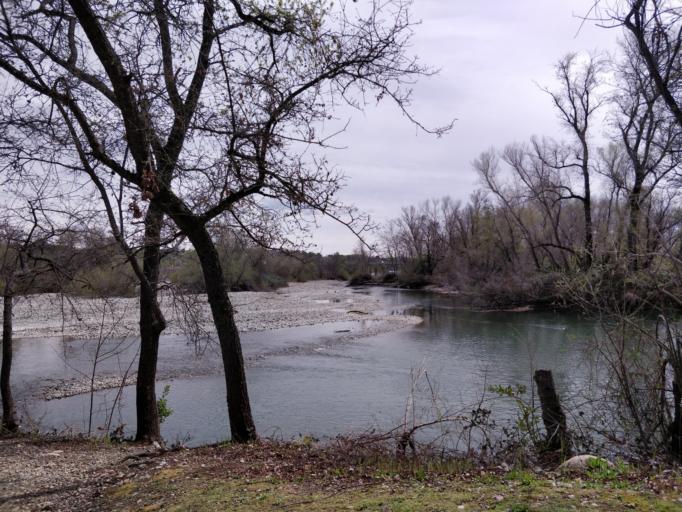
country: US
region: California
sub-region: Shasta County
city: Redding
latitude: 40.5895
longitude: -122.3708
